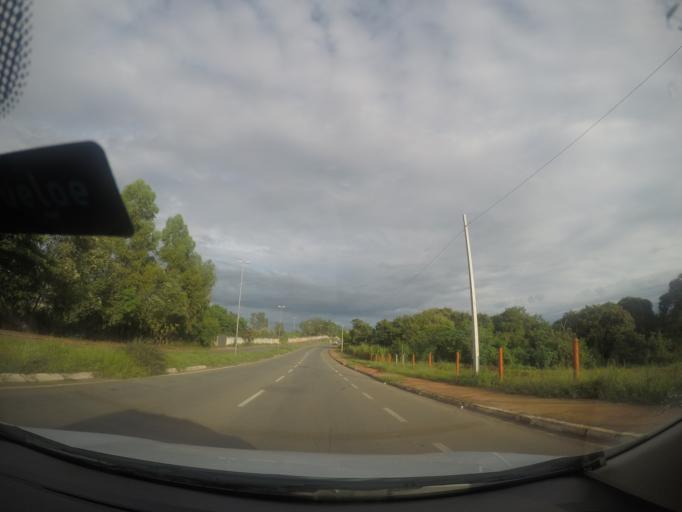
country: BR
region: Goias
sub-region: Goiania
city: Goiania
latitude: -16.6361
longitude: -49.3193
